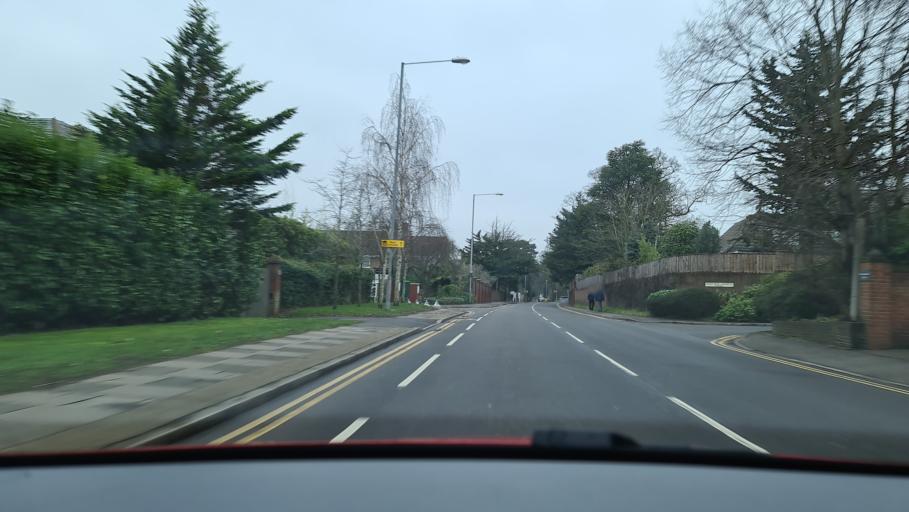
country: GB
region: England
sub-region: Greater London
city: New Malden
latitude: 51.4163
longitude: -0.2565
